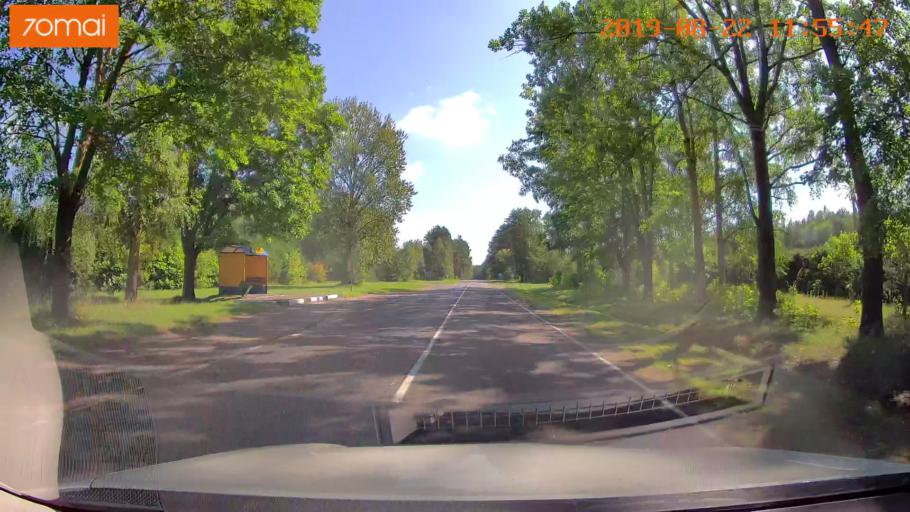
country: BY
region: Minsk
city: Prawdzinski
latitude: 53.4304
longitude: 27.5558
